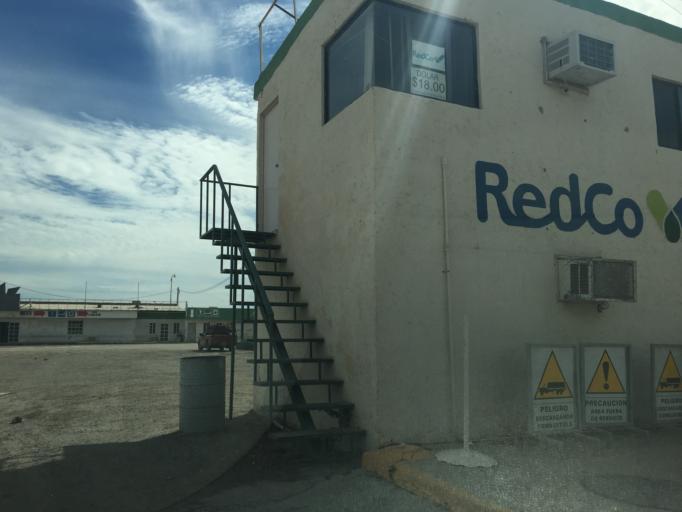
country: MX
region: Sonora
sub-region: Empalme
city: Empalme
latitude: 28.3200
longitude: -111.0429
